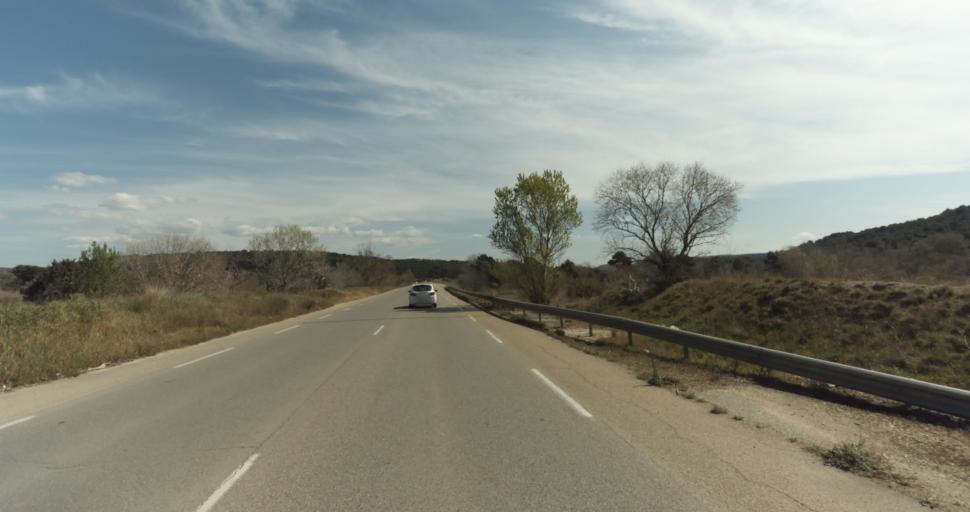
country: FR
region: Provence-Alpes-Cote d'Azur
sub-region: Departement des Bouches-du-Rhone
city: Coudoux
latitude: 43.5474
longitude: 5.2497
